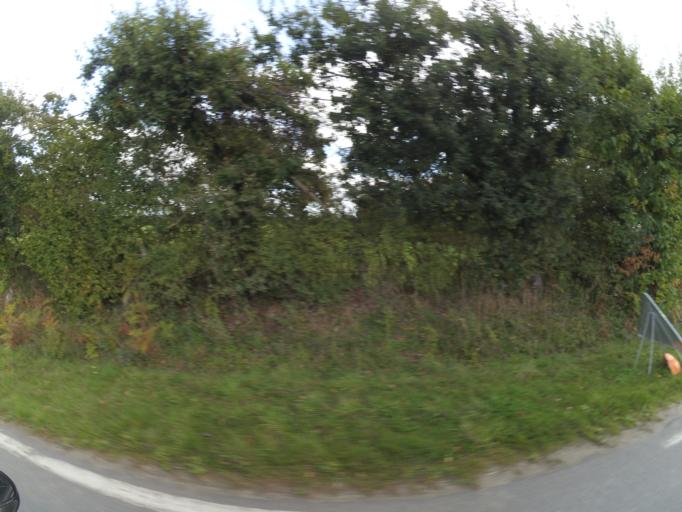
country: FR
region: Pays de la Loire
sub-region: Departement de la Loire-Atlantique
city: Suce-sur-Erdre
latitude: 47.3262
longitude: -1.5116
